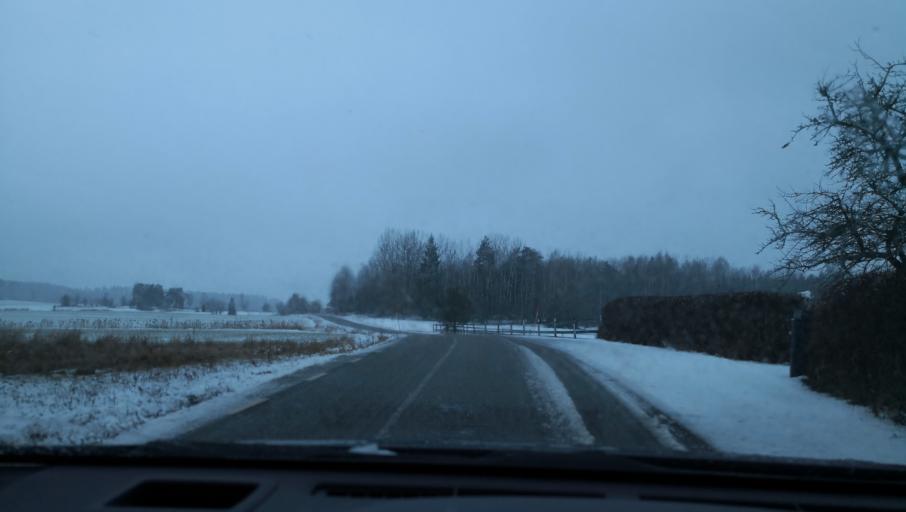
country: SE
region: Vaestmanland
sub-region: Kopings Kommun
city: Koping
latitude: 59.5784
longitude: 15.9711
